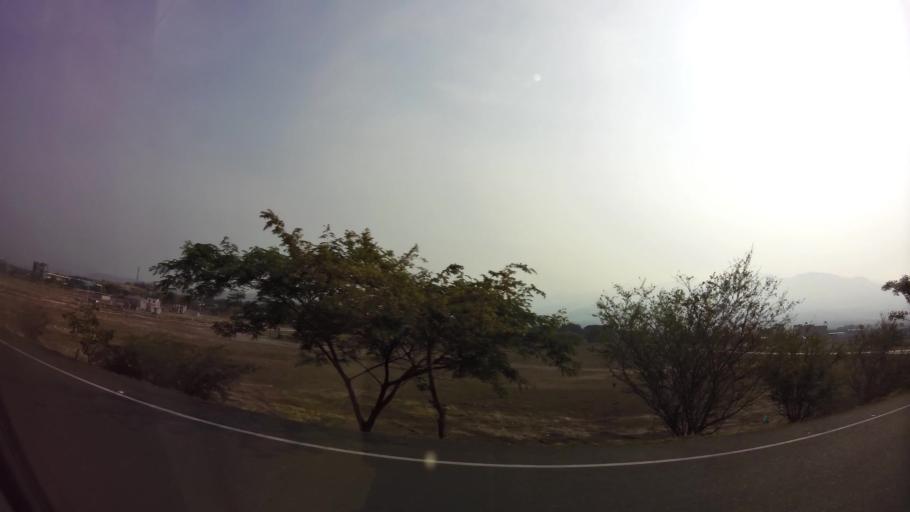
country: HN
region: Comayagua
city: Comayagua
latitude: 14.4246
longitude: -87.6324
